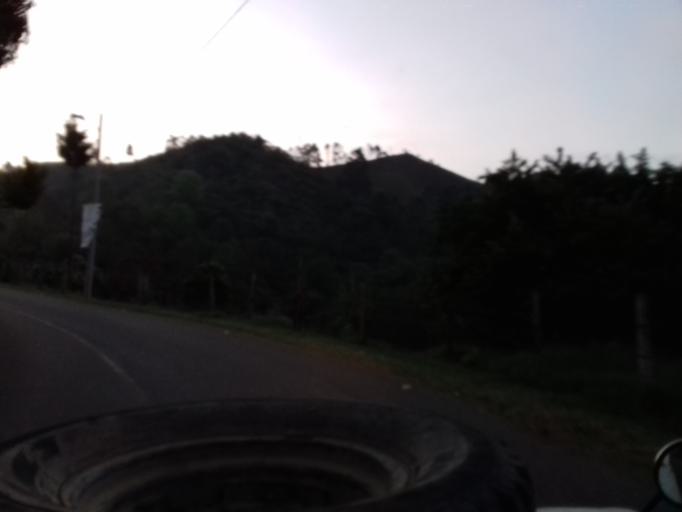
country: CO
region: Quindio
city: Salento
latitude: 4.6406
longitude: -75.5836
